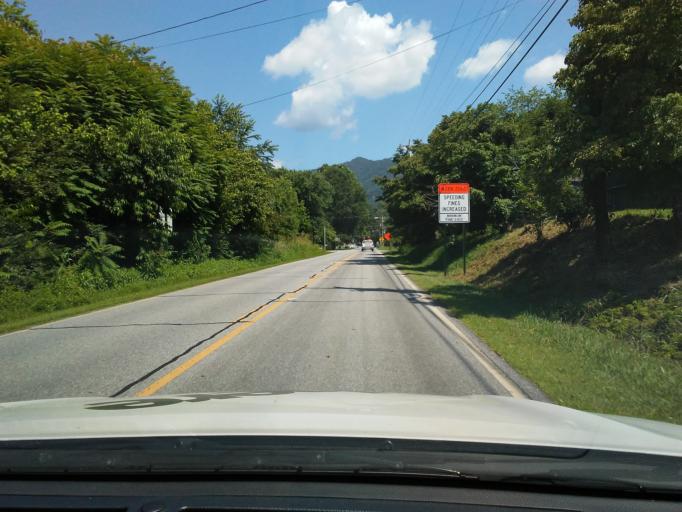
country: US
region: Georgia
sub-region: Towns County
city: Hiawassee
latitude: 34.9360
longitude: -83.8514
